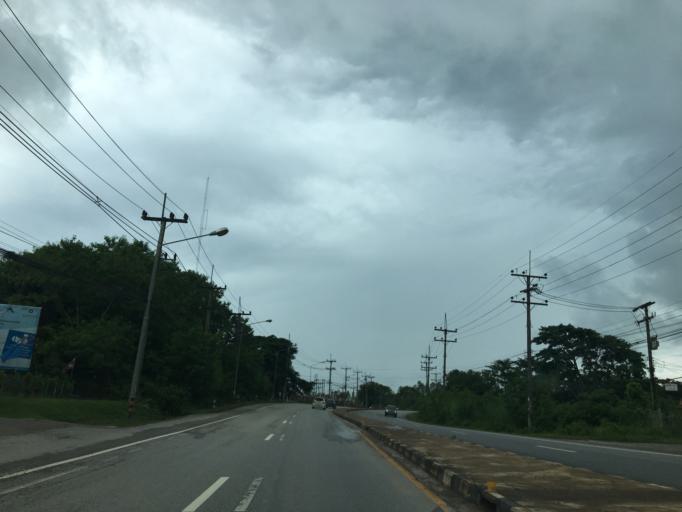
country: TH
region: Chiang Rai
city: Chiang Rai
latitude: 19.8486
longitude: 99.8601
